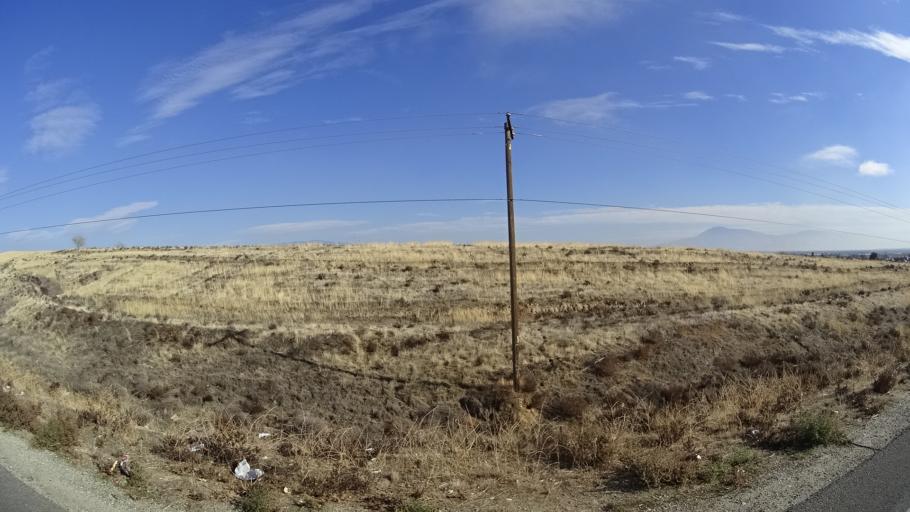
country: US
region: California
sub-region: Kern County
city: Bakersfield
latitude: 35.3852
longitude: -118.9143
